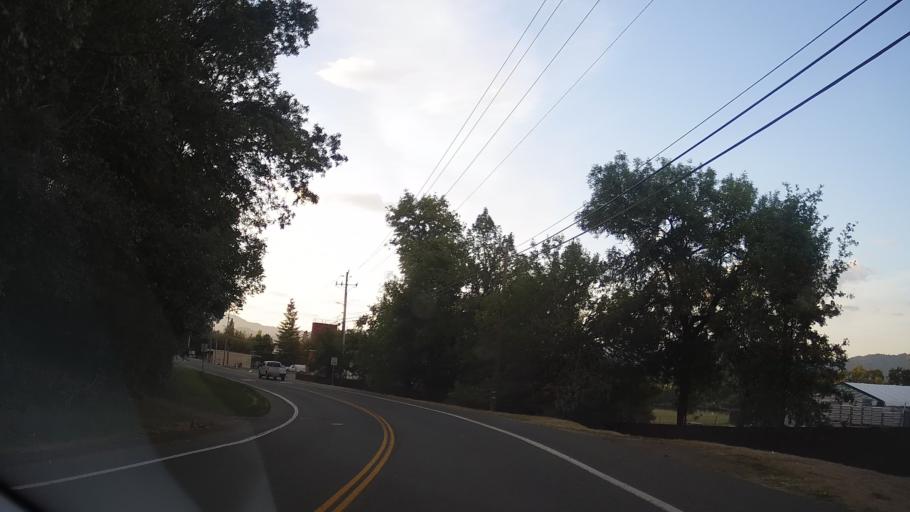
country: US
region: California
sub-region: Mendocino County
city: Willits
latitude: 39.3922
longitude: -123.3429
